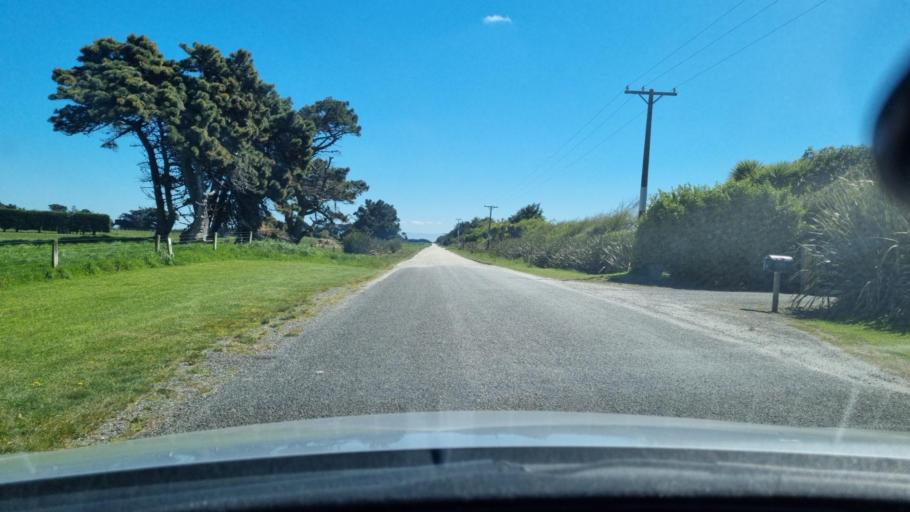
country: NZ
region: Southland
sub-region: Invercargill City
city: Invercargill
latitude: -46.4227
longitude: 168.2773
